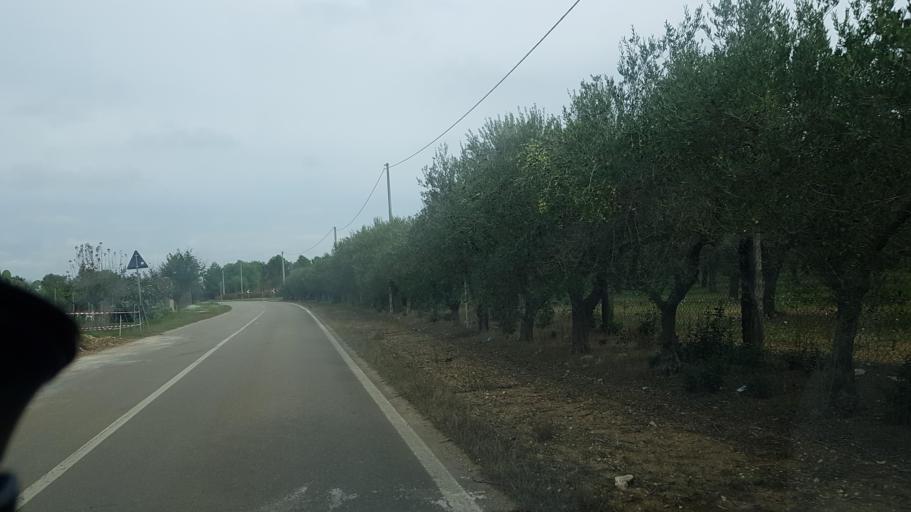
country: IT
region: Apulia
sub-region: Provincia di Lecce
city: Guagnano
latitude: 40.4143
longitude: 17.9496
